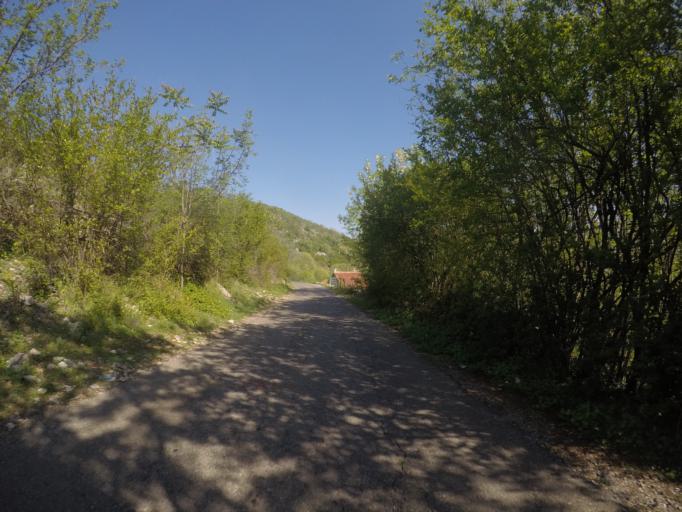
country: ME
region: Danilovgrad
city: Danilovgrad
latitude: 42.5328
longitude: 19.0900
